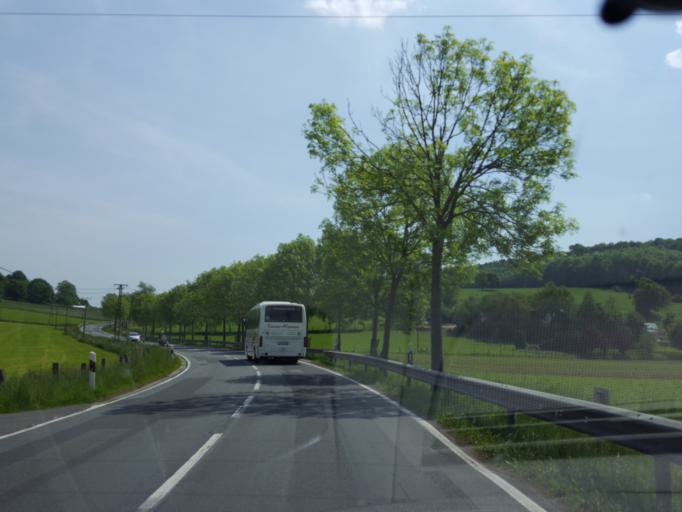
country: DE
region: North Rhine-Westphalia
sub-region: Regierungsbezirk Arnsberg
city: Brilon
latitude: 51.4050
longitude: 8.6118
